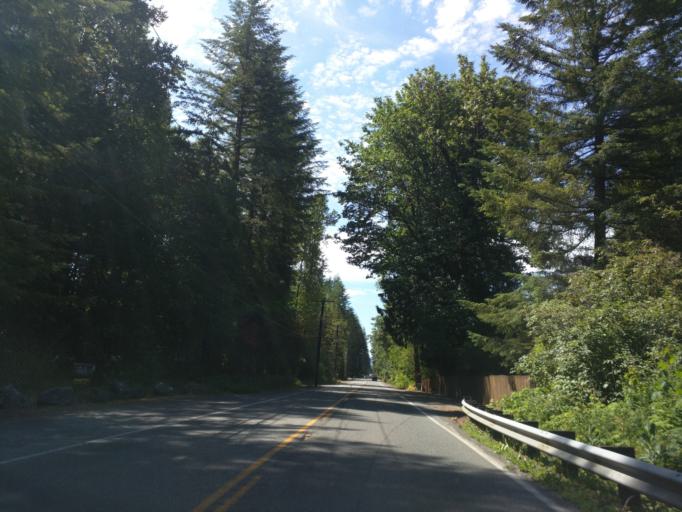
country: US
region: Washington
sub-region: Whatcom County
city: Peaceful Valley
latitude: 48.9336
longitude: -122.1435
